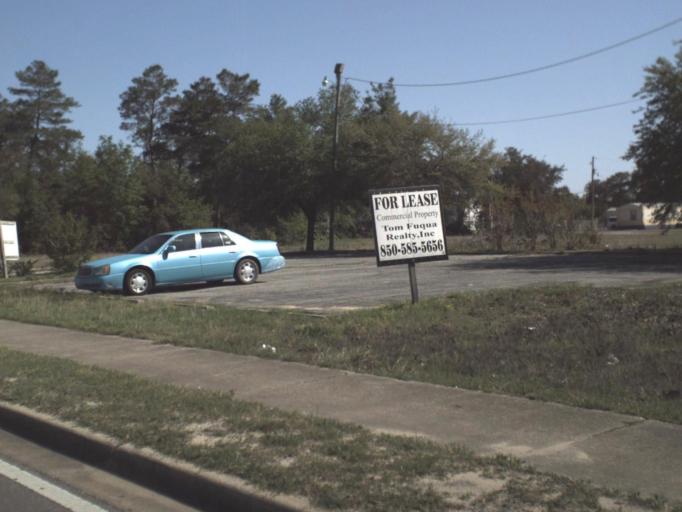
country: US
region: Florida
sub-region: Okaloosa County
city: Ocean City
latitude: 30.4454
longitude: -86.6062
